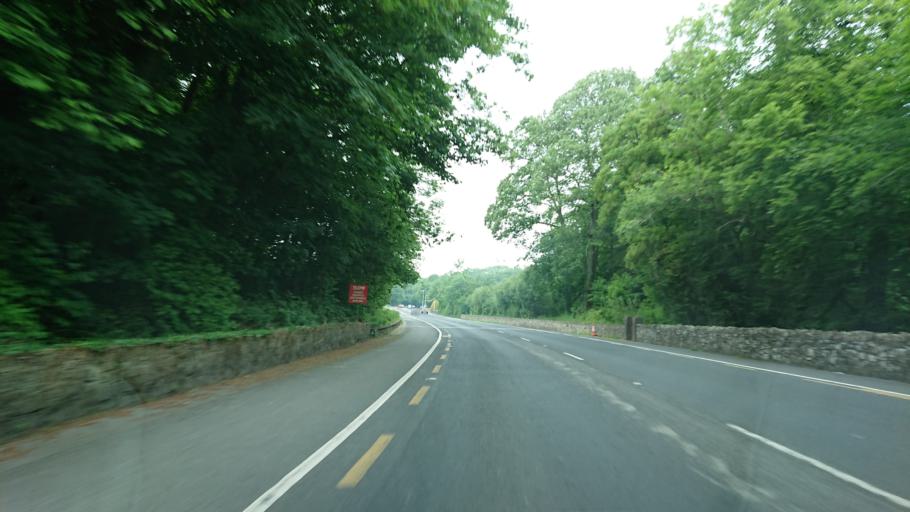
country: IE
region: Munster
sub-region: Waterford
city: Waterford
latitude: 52.2127
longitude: -7.1192
